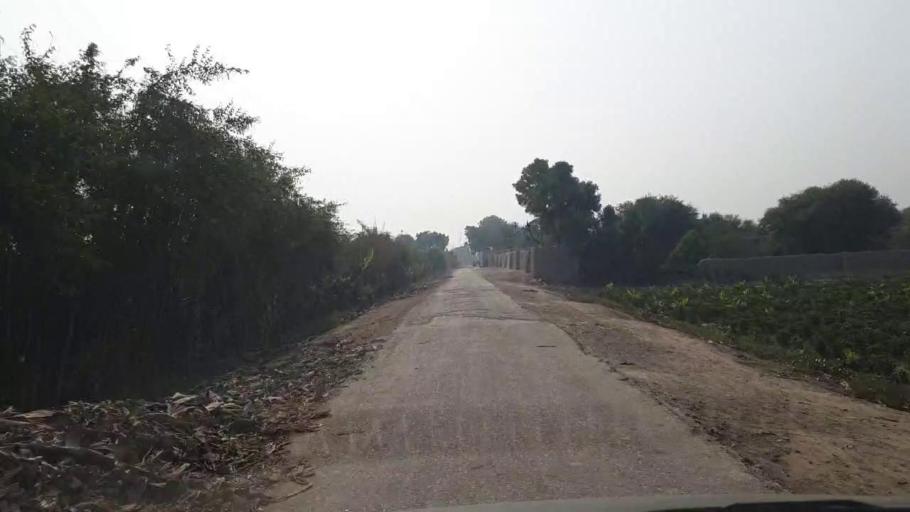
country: PK
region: Sindh
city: Hala
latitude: 25.8159
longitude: 68.4375
